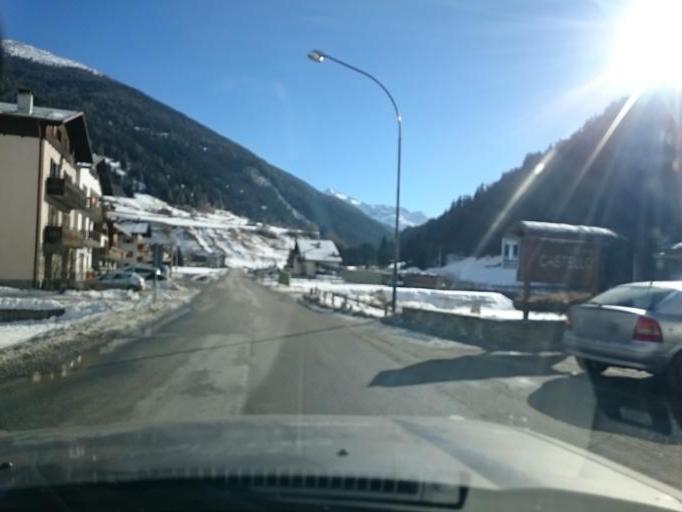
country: IT
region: Lombardy
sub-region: Provincia di Sondrio
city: Sant'Antonio
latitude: 46.4576
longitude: 10.4264
